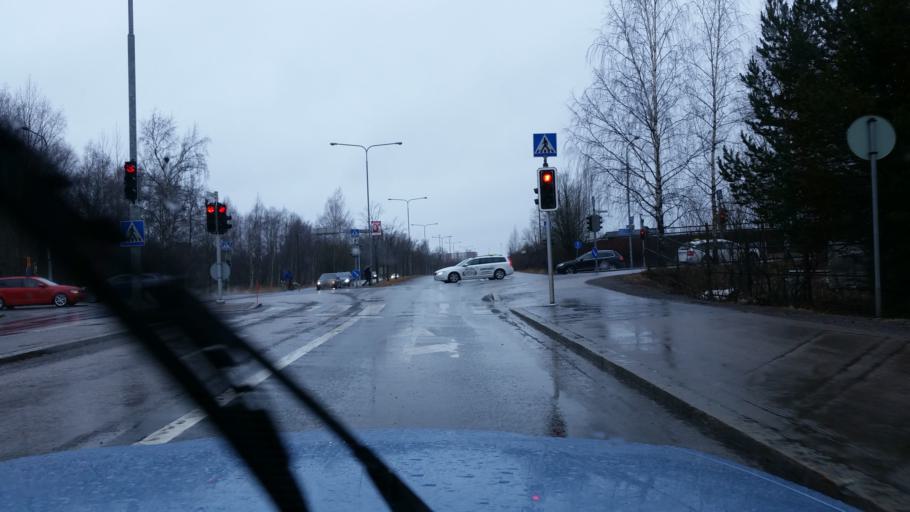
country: FI
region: Pirkanmaa
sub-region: Tampere
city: Tampere
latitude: 61.4751
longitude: 23.7839
